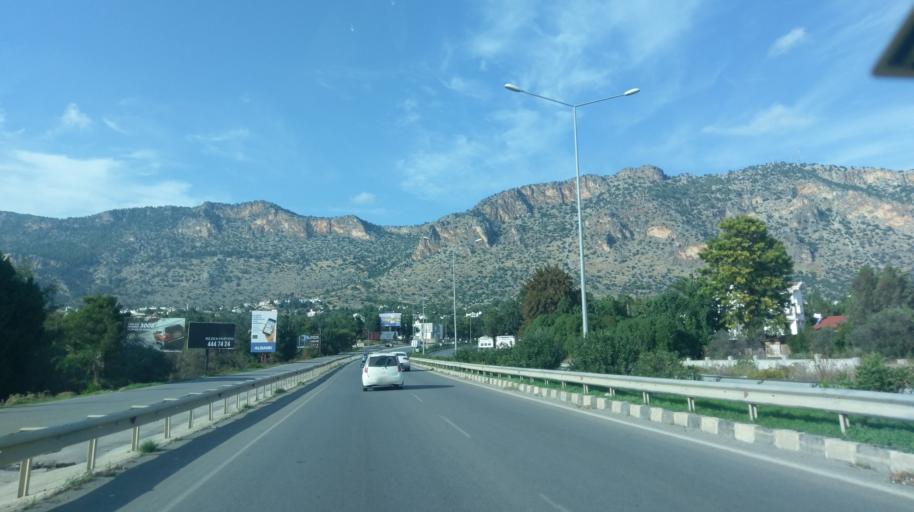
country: CY
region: Keryneia
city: Kyrenia
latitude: 35.2882
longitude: 33.2772
